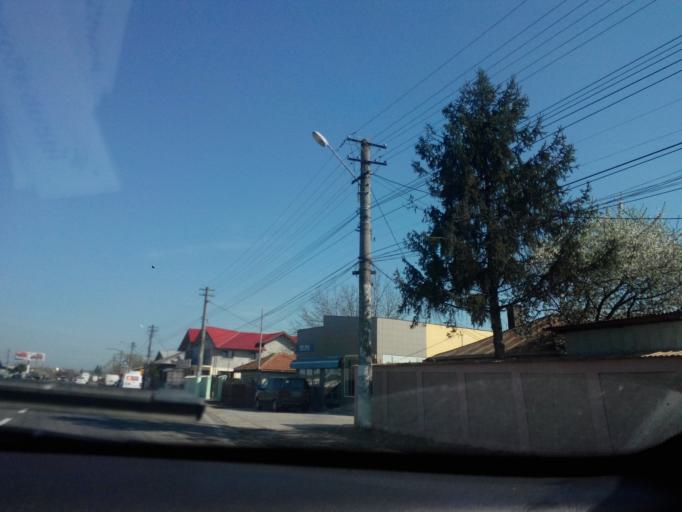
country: RO
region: Prahova
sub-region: Comuna Puchenii Mari
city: Miroslavesti
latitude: 44.8057
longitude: 26.0848
